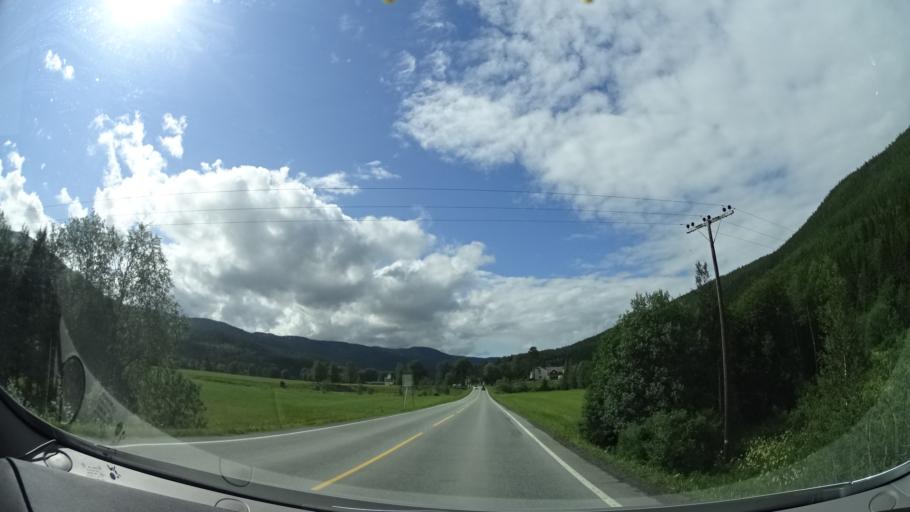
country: NO
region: Nord-Trondelag
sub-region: Meraker
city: Meraker
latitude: 63.4436
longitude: 11.6580
